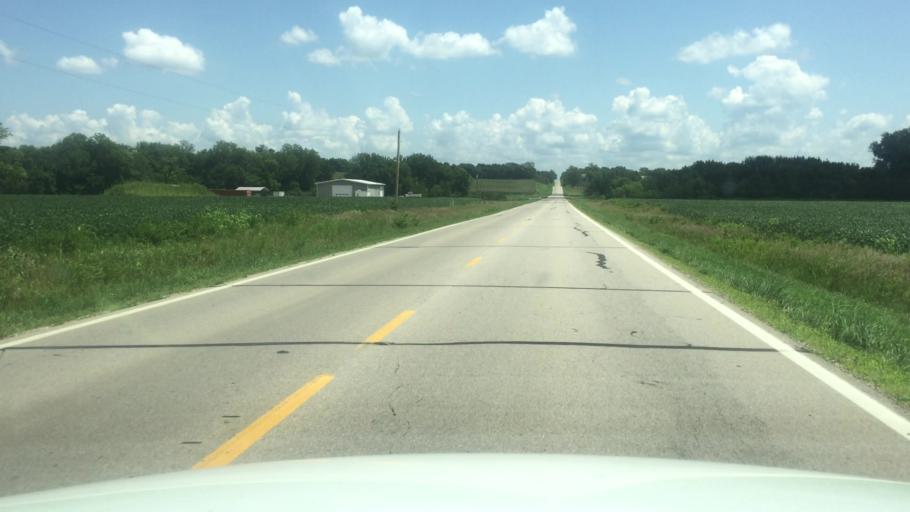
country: US
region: Kansas
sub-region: Brown County
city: Horton
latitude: 39.6673
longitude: -95.5519
